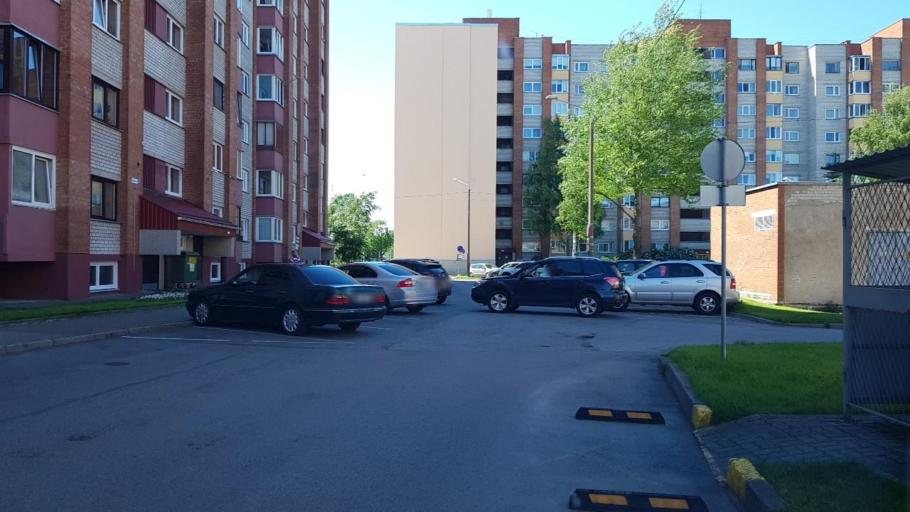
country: EE
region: Ida-Virumaa
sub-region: Narva linn
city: Narva
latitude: 59.3839
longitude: 28.1640
